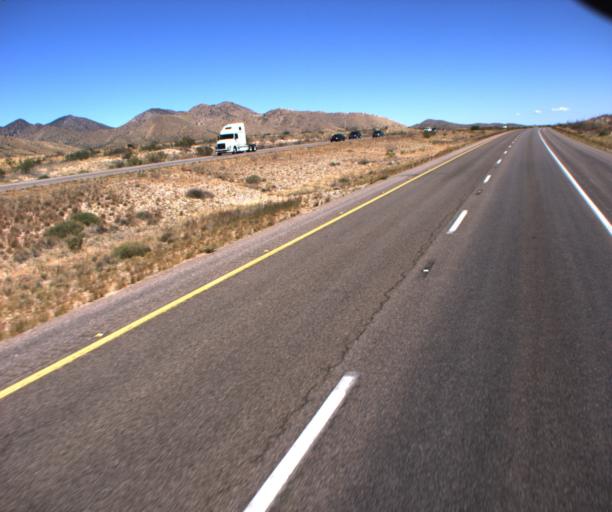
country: US
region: Arizona
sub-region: Cochise County
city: Whetstone
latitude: 31.8000
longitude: -110.3499
